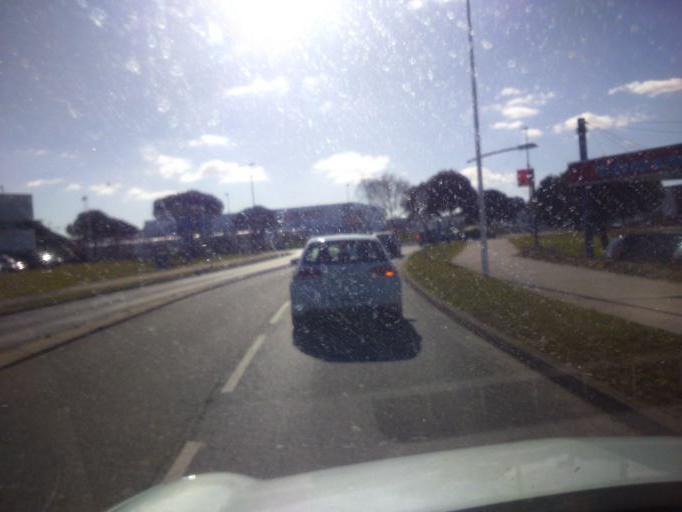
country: FR
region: Pays de la Loire
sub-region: Departement de la Loire-Atlantique
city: Guerande
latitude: 47.3279
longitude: -2.4128
